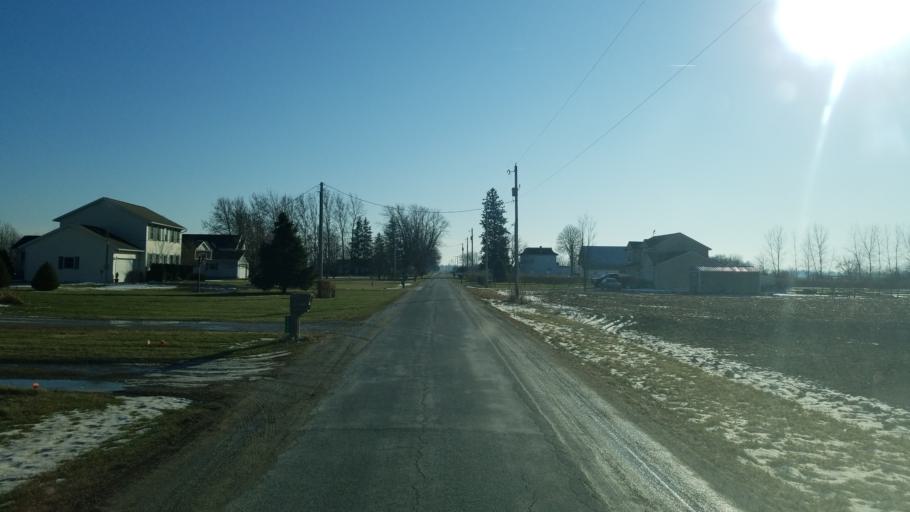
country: US
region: Ohio
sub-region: Sandusky County
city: Mount Carmel
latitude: 41.2942
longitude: -82.9413
